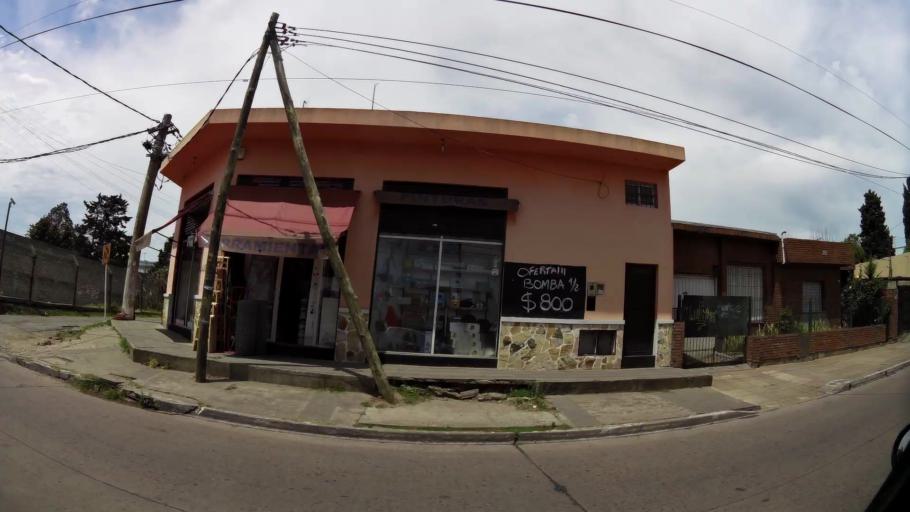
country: AR
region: Buenos Aires
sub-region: Partido de Quilmes
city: Quilmes
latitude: -34.7775
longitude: -58.2566
